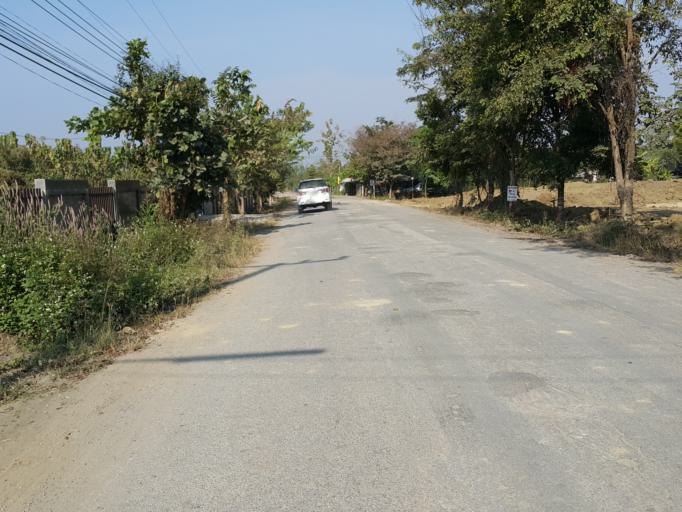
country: TH
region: Chiang Mai
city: San Kamphaeng
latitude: 18.6964
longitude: 99.1119
